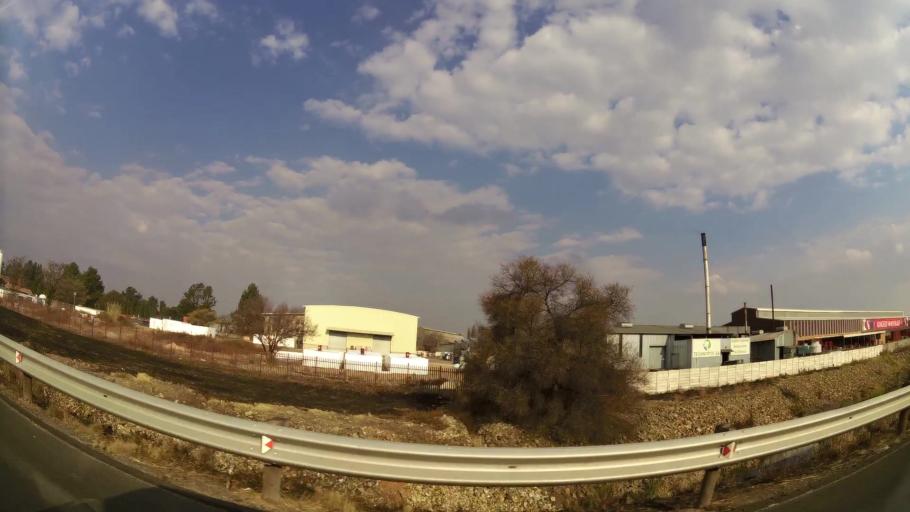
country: ZA
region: Gauteng
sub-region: Ekurhuleni Metropolitan Municipality
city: Springs
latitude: -26.2779
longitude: 28.4568
